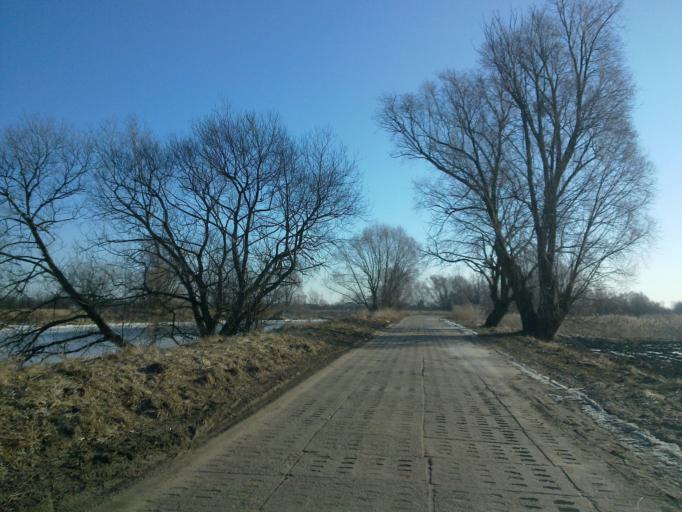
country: PL
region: Pomeranian Voivodeship
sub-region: Gdansk
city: Gdansk
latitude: 54.3243
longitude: 18.6599
